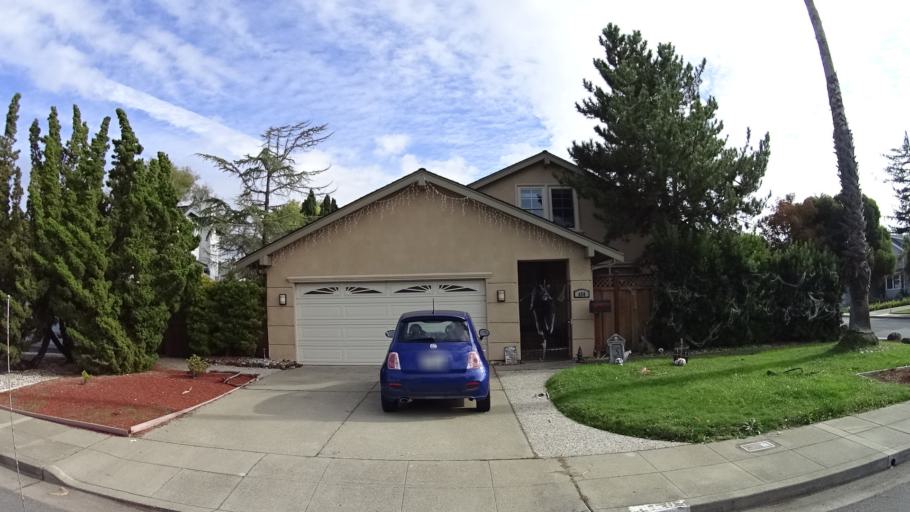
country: US
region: California
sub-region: San Mateo County
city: Redwood Shores
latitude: 37.5280
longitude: -122.2518
